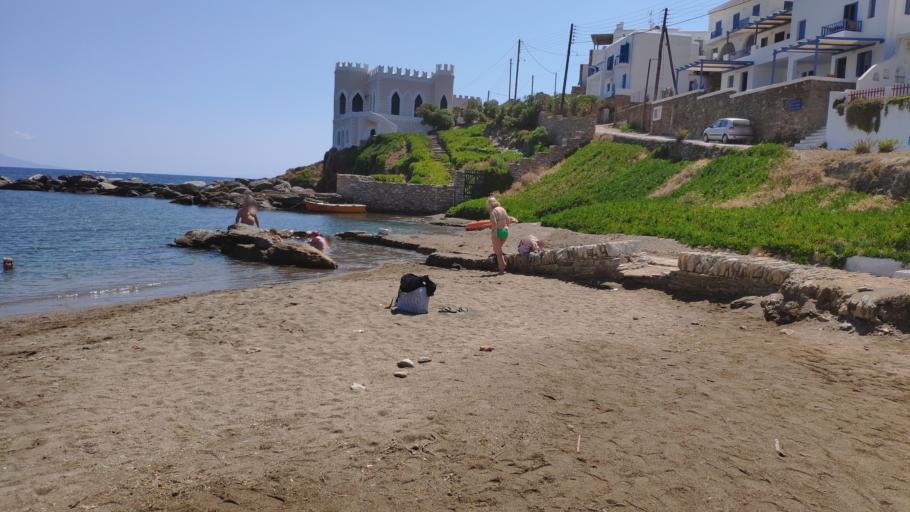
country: GR
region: South Aegean
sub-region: Nomos Kykladon
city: Kythnos
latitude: 37.4412
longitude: 24.4259
